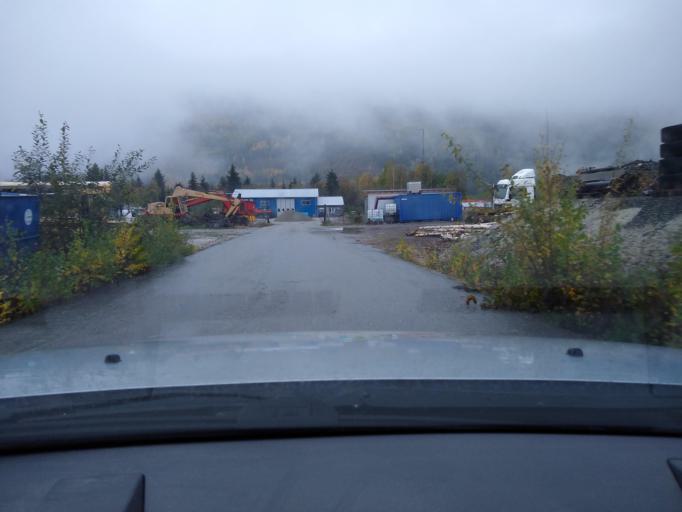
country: NO
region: Oppland
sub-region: Ringebu
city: Ringebu
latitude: 61.5439
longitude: 10.0577
